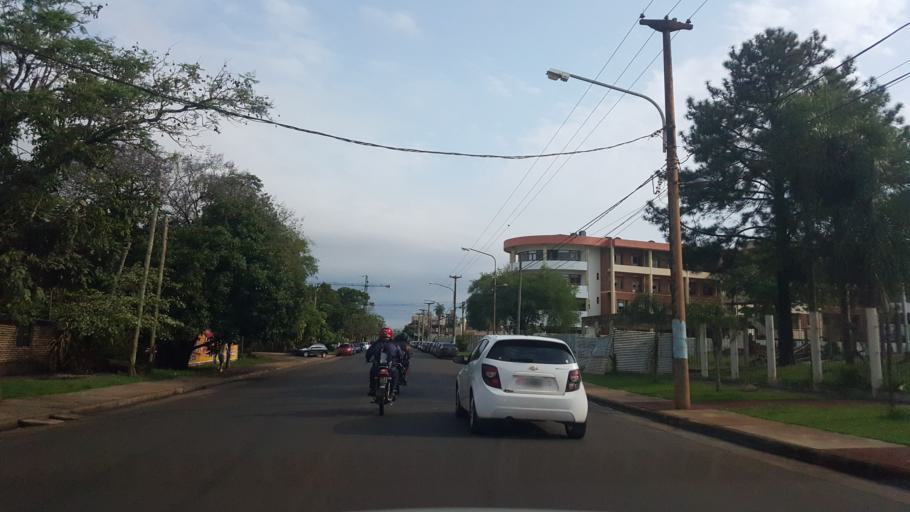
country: AR
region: Misiones
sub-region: Departamento de Capital
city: Posadas
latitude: -27.3834
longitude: -55.8884
